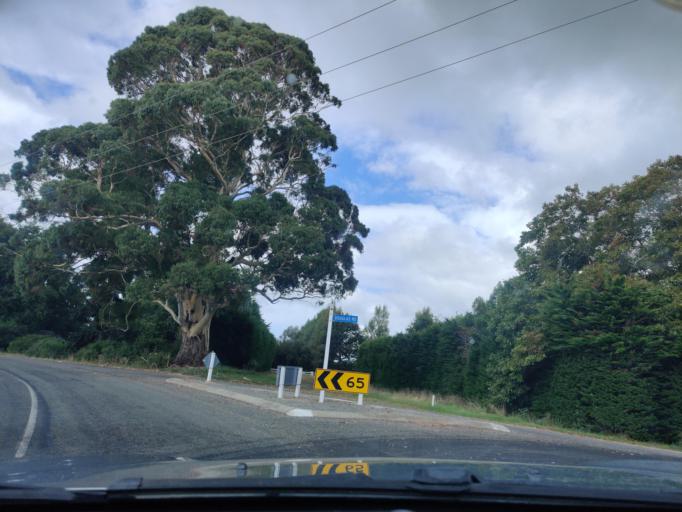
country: NZ
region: Canterbury
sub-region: Hurunui District
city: Amberley
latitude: -43.1278
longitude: 172.6880
